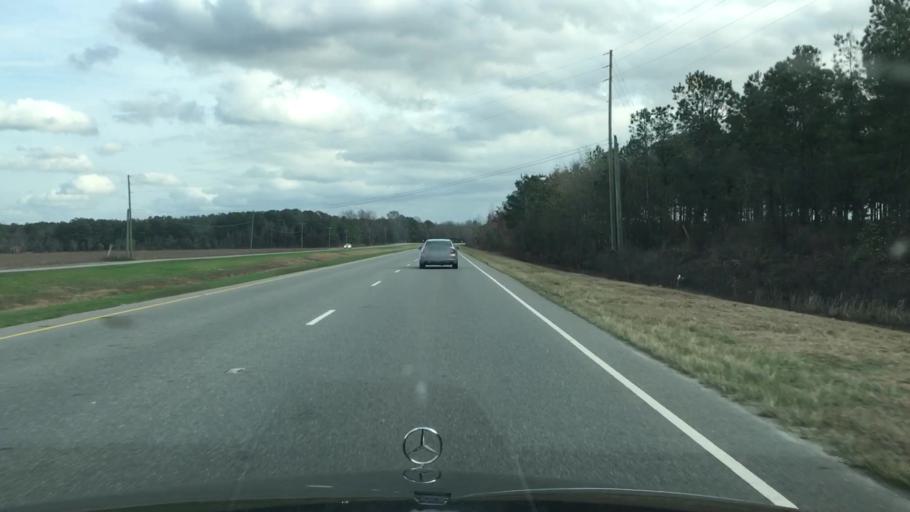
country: US
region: North Carolina
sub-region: Duplin County
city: Kenansville
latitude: 34.9489
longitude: -77.8852
